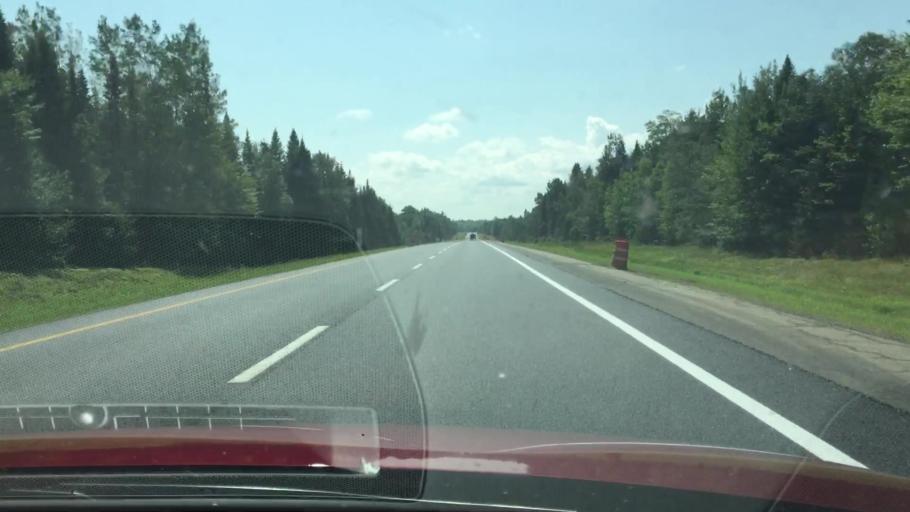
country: US
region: Maine
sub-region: Penobscot County
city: Patten
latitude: 45.8550
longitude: -68.4251
